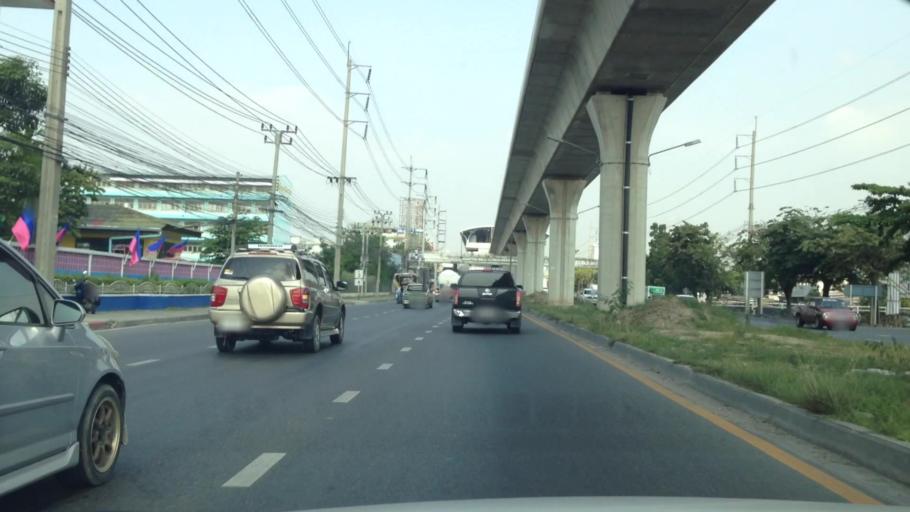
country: TH
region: Samut Prakan
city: Samut Prakan
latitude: 13.5647
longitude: 100.6091
